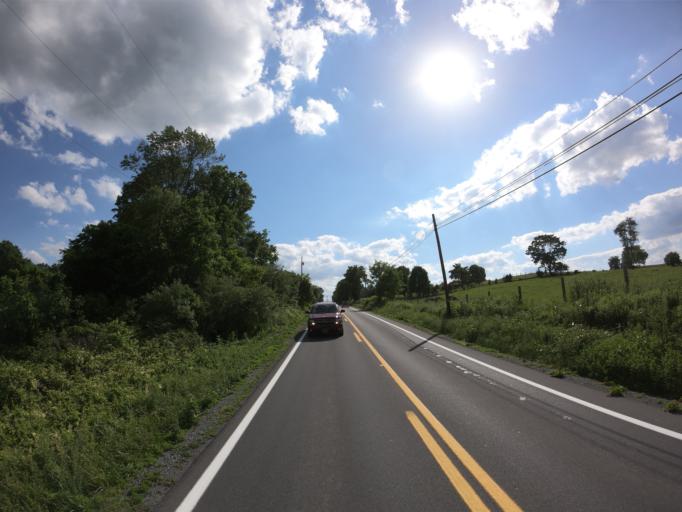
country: US
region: West Virginia
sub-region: Jefferson County
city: Shepherdstown
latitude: 39.4068
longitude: -77.8575
